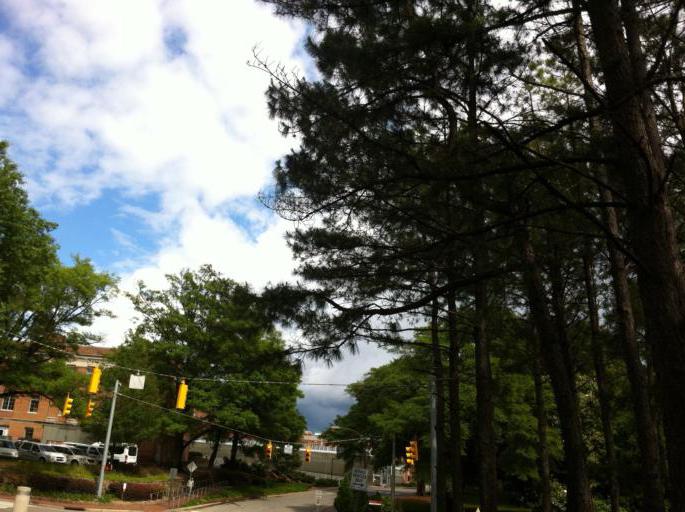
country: US
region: North Carolina
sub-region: Wake County
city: West Raleigh
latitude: 35.7870
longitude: -78.6752
